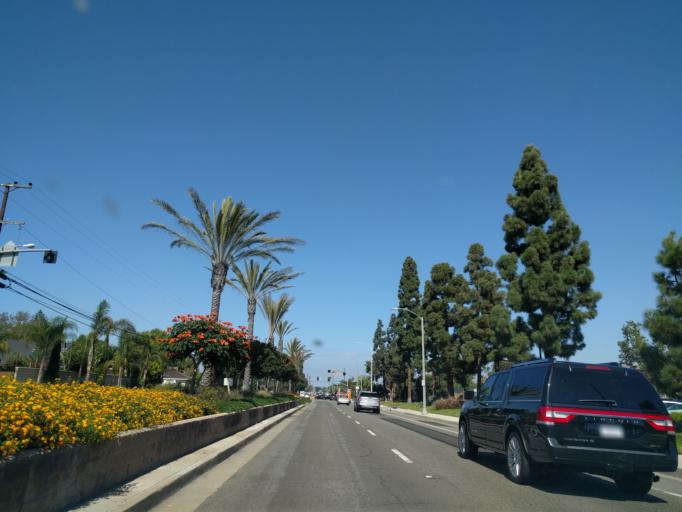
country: US
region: California
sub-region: Orange County
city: Costa Mesa
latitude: 33.6327
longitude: -117.9043
